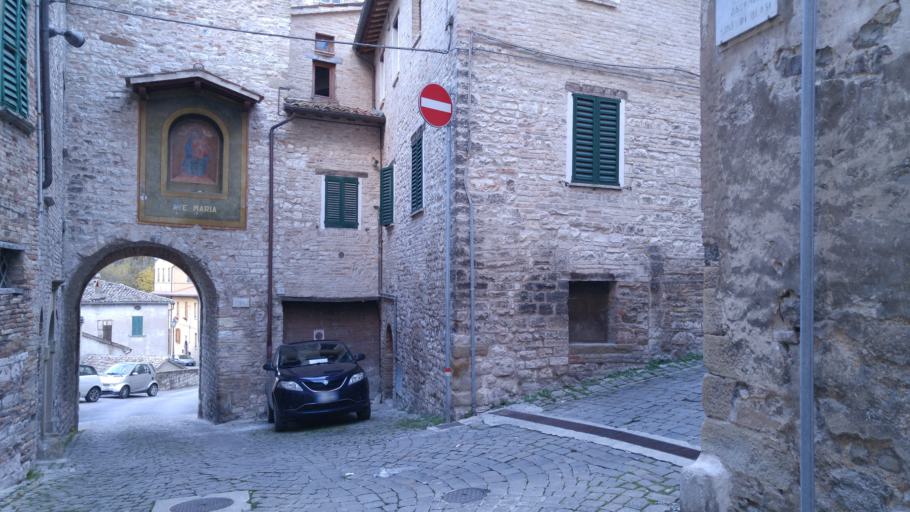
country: IT
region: The Marches
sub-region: Provincia di Pesaro e Urbino
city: Pergola
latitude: 43.5629
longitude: 12.8375
